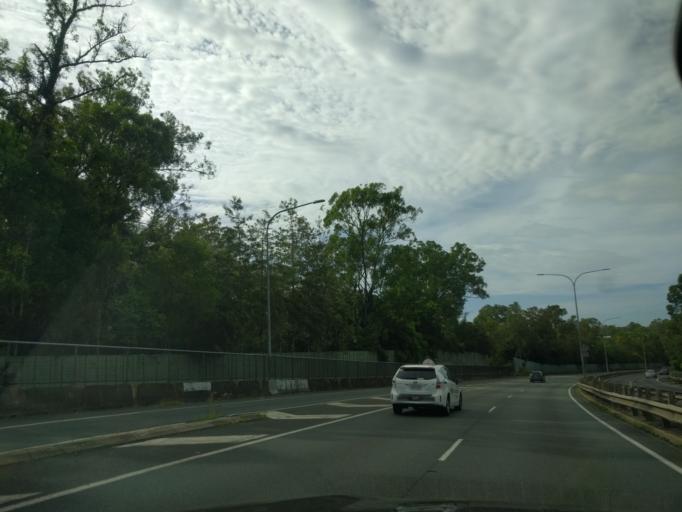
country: AU
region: Queensland
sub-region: Brisbane
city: Taringa
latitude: -27.5041
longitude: 152.9634
